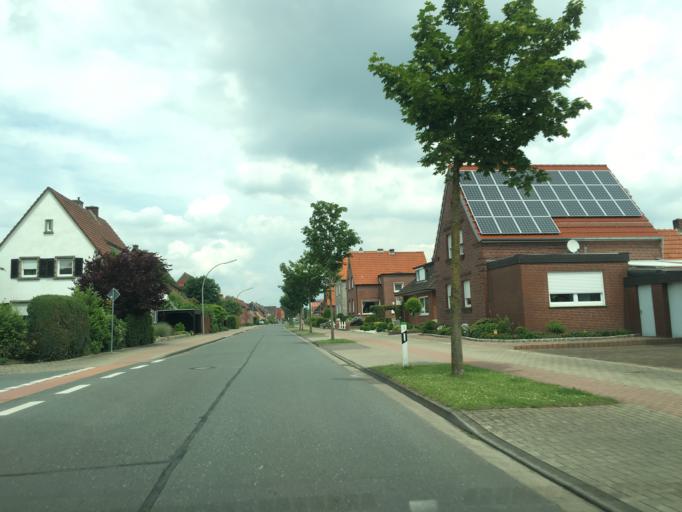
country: DE
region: North Rhine-Westphalia
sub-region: Regierungsbezirk Munster
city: Laer
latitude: 52.1063
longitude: 7.3968
